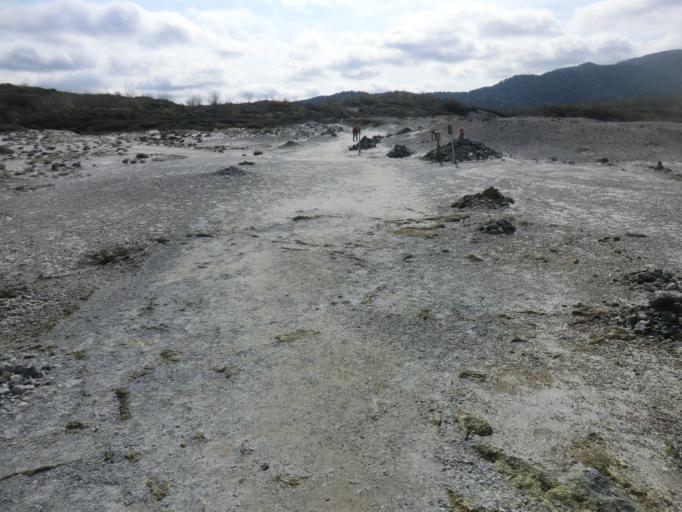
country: JP
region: Aomori
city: Mutsu
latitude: 41.3269
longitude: 141.0860
